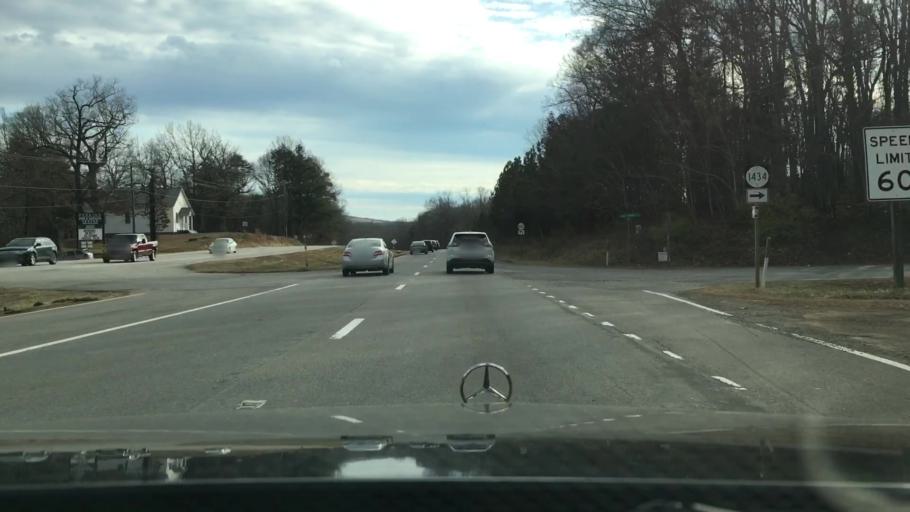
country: US
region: Virginia
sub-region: Pittsylvania County
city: Chatham
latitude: 36.7854
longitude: -79.3942
